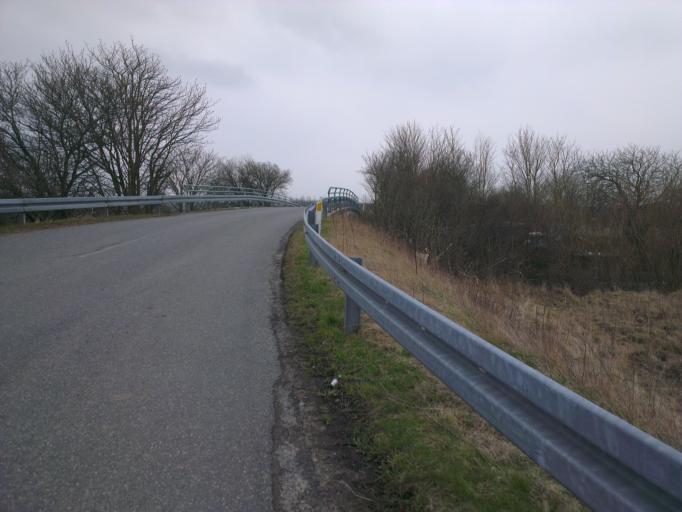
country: DK
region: Capital Region
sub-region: Egedal Kommune
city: Olstykke
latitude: 55.8335
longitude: 12.1383
